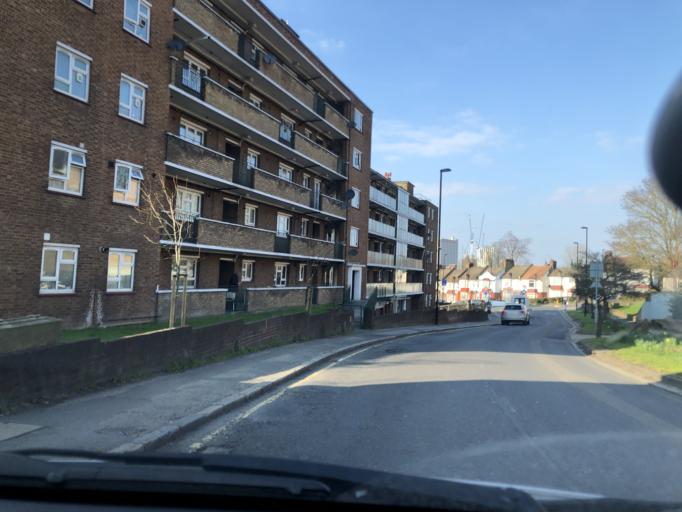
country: GB
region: England
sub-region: Greater London
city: Catford
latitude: 51.4553
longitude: -0.0098
